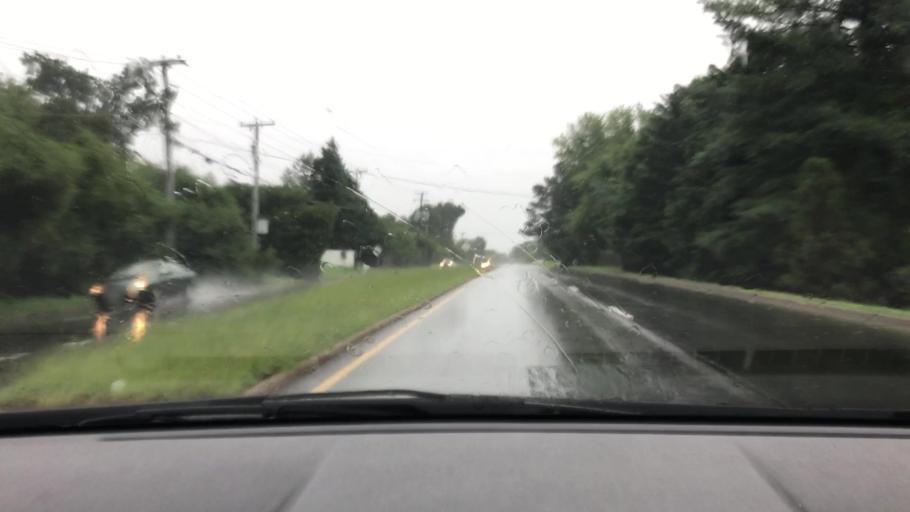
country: US
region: Virginia
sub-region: Henrico County
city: Laurel
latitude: 37.6490
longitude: -77.5533
